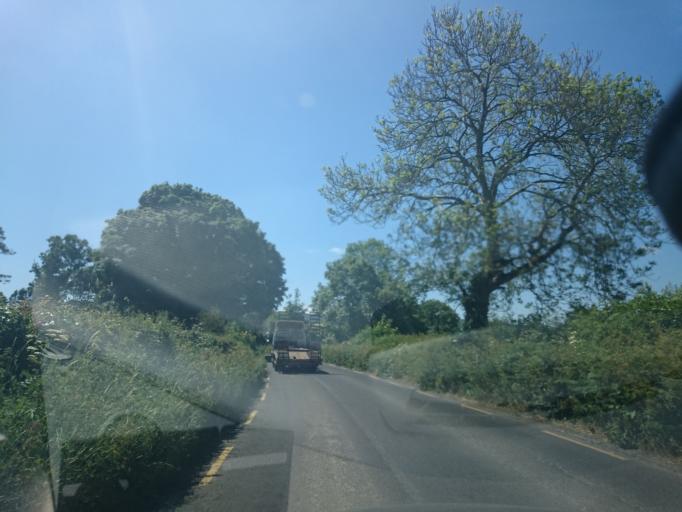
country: IE
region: Leinster
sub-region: Kilkenny
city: Graiguenamanagh
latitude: 52.6015
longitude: -6.9926
